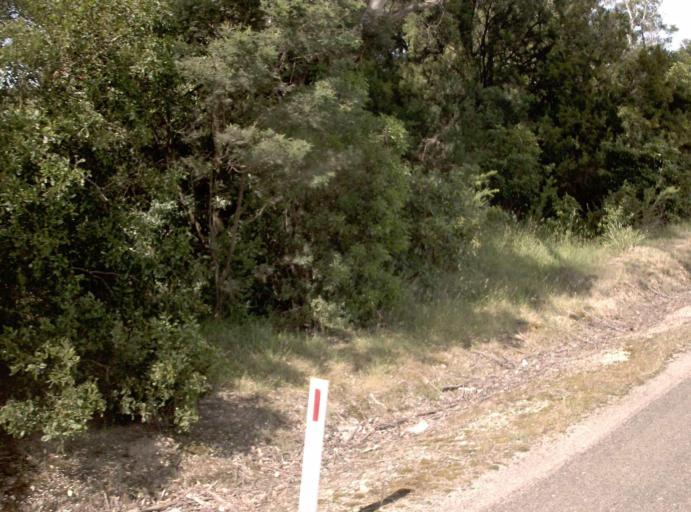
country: AU
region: Victoria
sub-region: East Gippsland
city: Lakes Entrance
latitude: -37.8224
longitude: 147.8490
